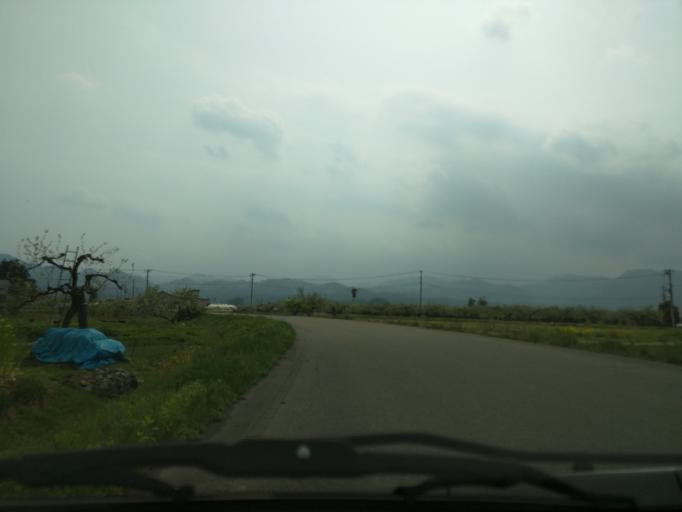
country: JP
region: Fukushima
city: Kitakata
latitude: 37.4438
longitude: 139.8459
